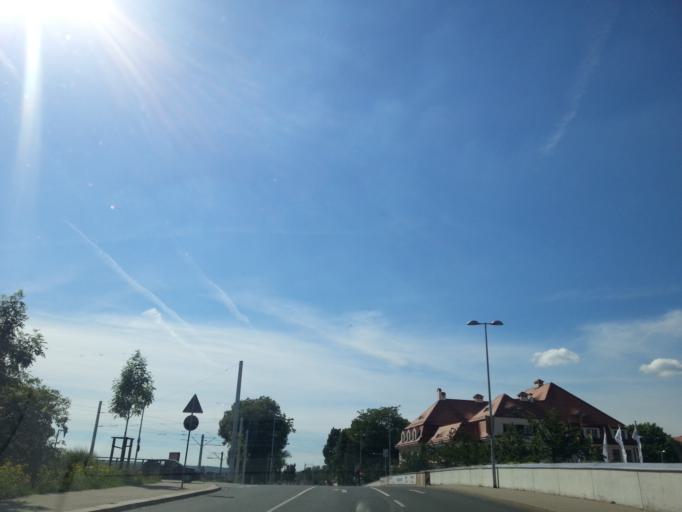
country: DE
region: Saxony
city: Dresden
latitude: 51.0683
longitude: 13.7175
